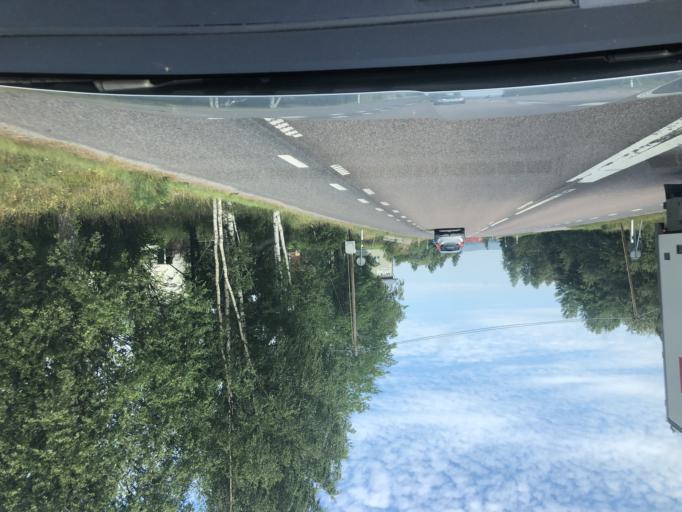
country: SE
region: Vaesternorrland
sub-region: Kramfors Kommun
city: Kramfors
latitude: 62.9048
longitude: 17.8276
